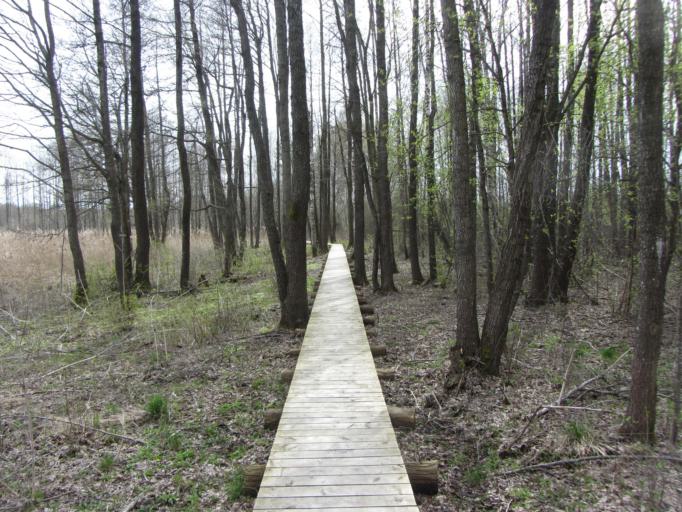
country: LT
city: Zarasai
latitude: 55.5780
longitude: 26.1500
